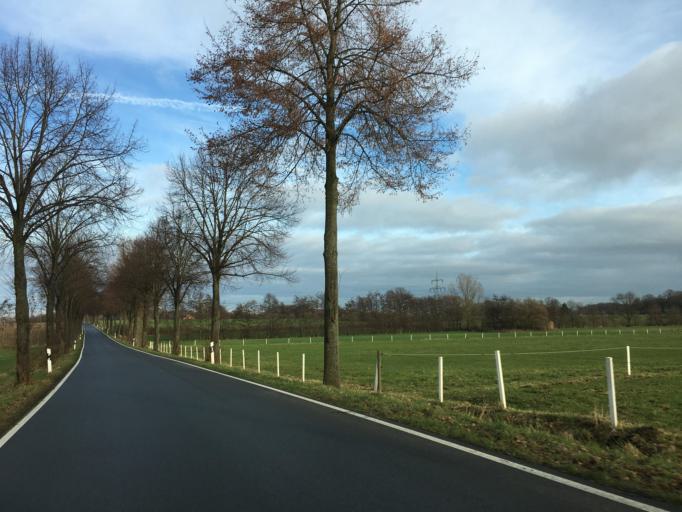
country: DE
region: North Rhine-Westphalia
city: Olfen
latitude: 51.7861
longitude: 7.3658
